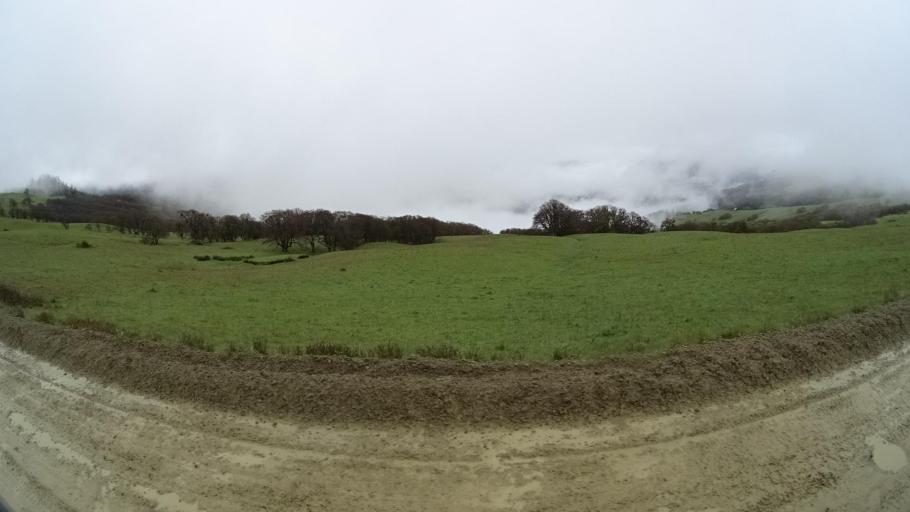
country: US
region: California
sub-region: Humboldt County
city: Westhaven-Moonstone
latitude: 41.1466
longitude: -123.8707
